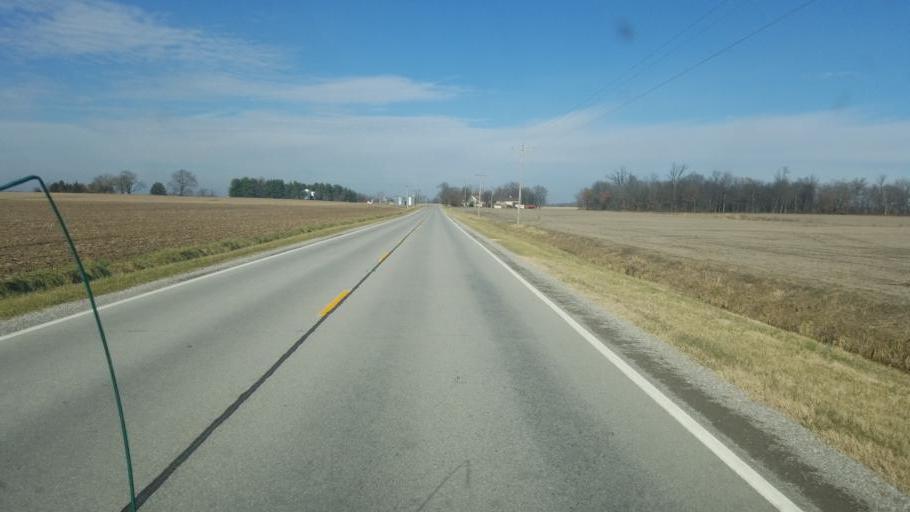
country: US
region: Illinois
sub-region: Saline County
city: Eldorado
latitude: 37.8951
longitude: -88.4530
